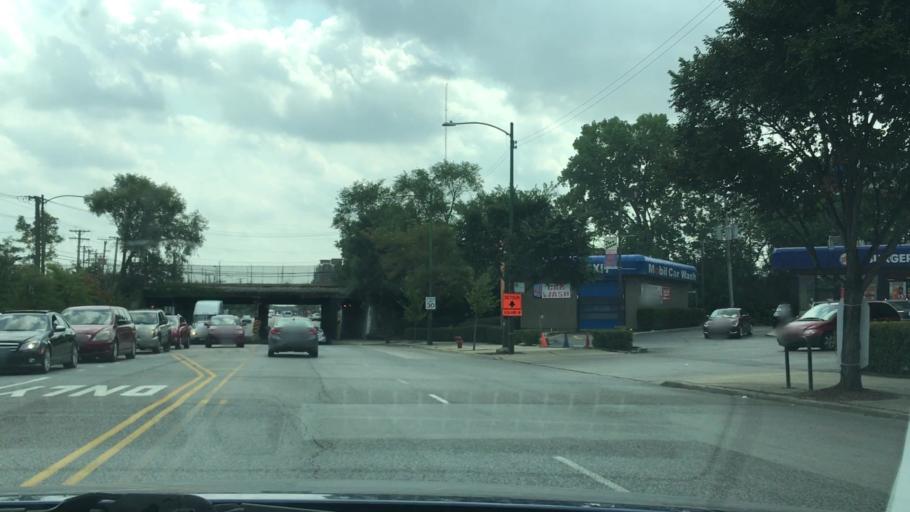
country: US
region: Illinois
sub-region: Cook County
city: Chicago
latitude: 41.8645
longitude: -87.6860
